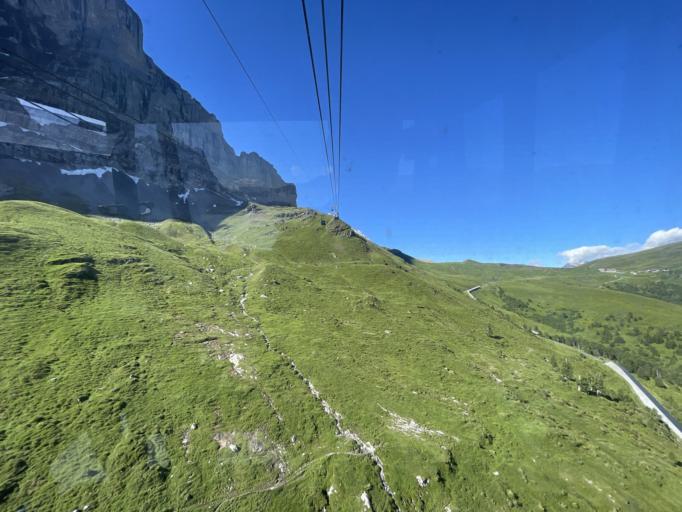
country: CH
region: Bern
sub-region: Interlaken-Oberhasli District
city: Grindelwald
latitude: 46.5895
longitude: 7.9882
